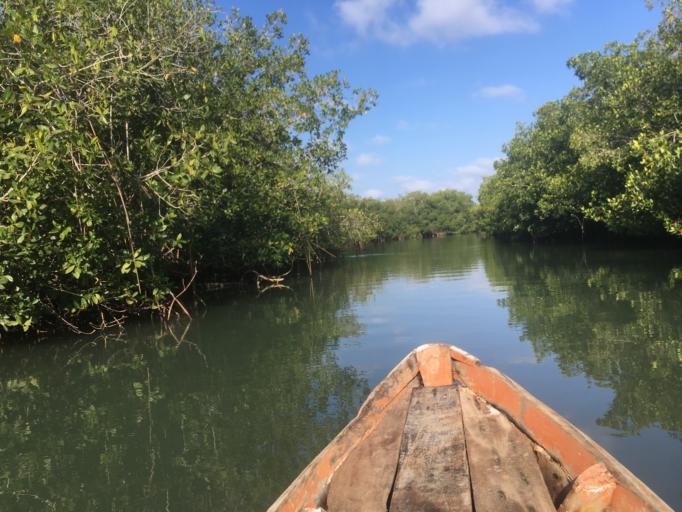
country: CO
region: Bolivar
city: Cartagena
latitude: 10.4903
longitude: -75.4851
